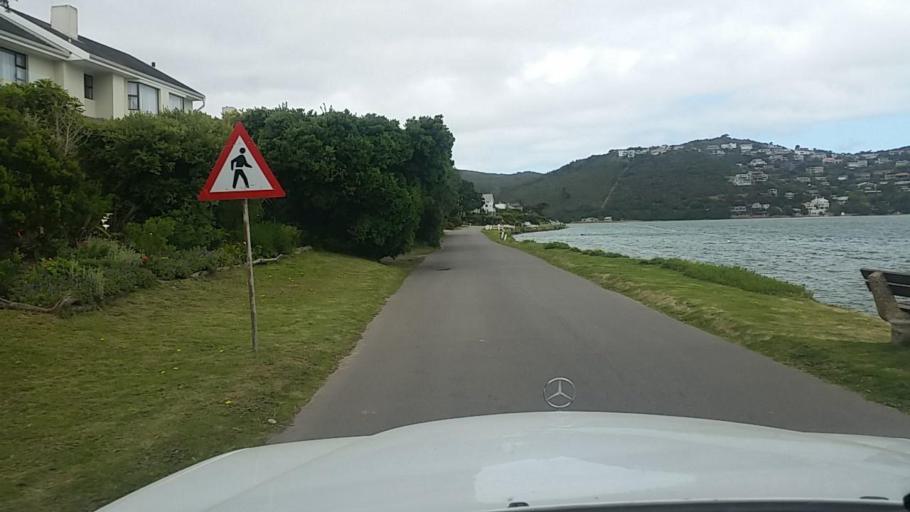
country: ZA
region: Western Cape
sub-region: Eden District Municipality
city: Knysna
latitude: -34.0683
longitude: 23.0569
